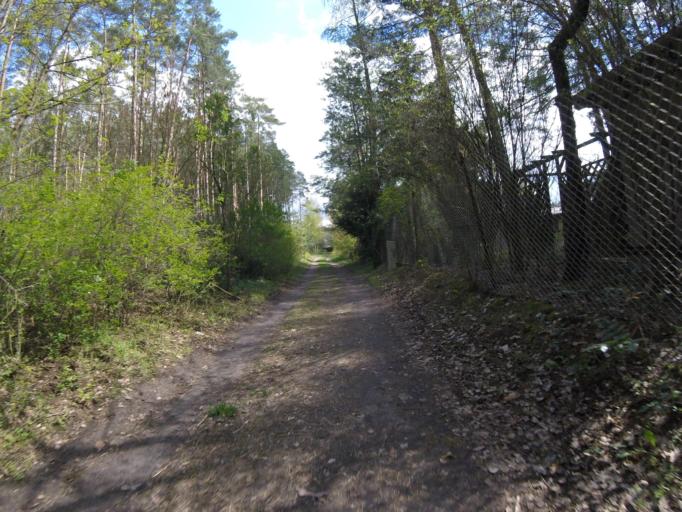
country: DE
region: Brandenburg
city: Bestensee
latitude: 52.2639
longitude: 13.6612
